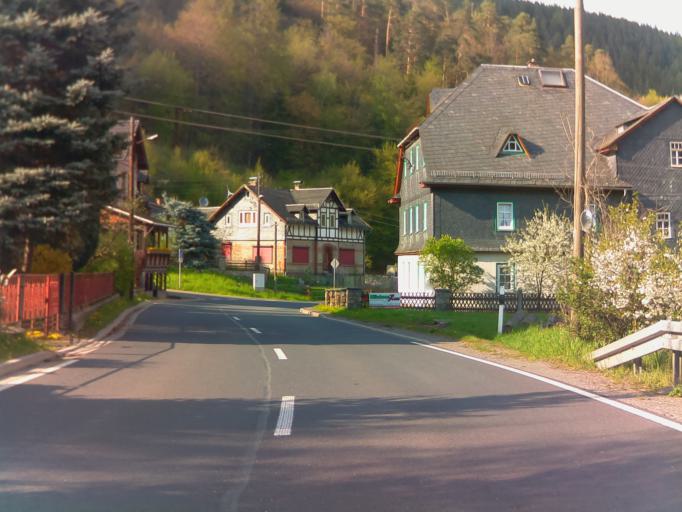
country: DE
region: Thuringia
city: Probstzella
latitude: 50.5769
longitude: 11.3746
